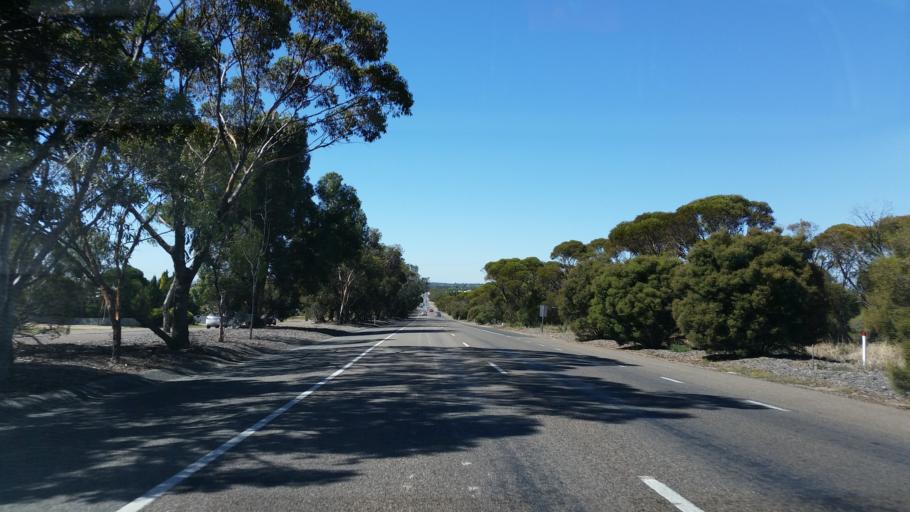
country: AU
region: South Australia
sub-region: Murray Bridge
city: Murray Bridge
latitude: -35.1354
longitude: 139.2353
